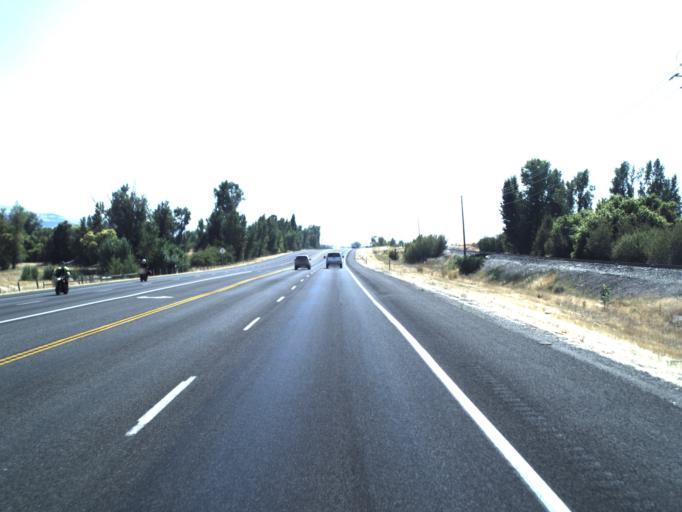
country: US
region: Utah
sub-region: Cache County
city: Richmond
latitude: 41.9586
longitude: -111.8130
